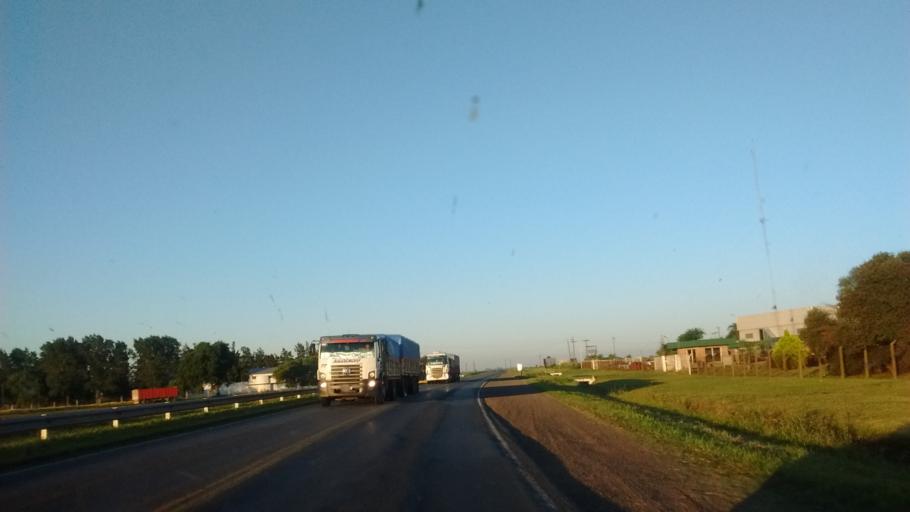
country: AR
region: Santa Fe
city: Casilda
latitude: -33.0752
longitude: -61.1980
